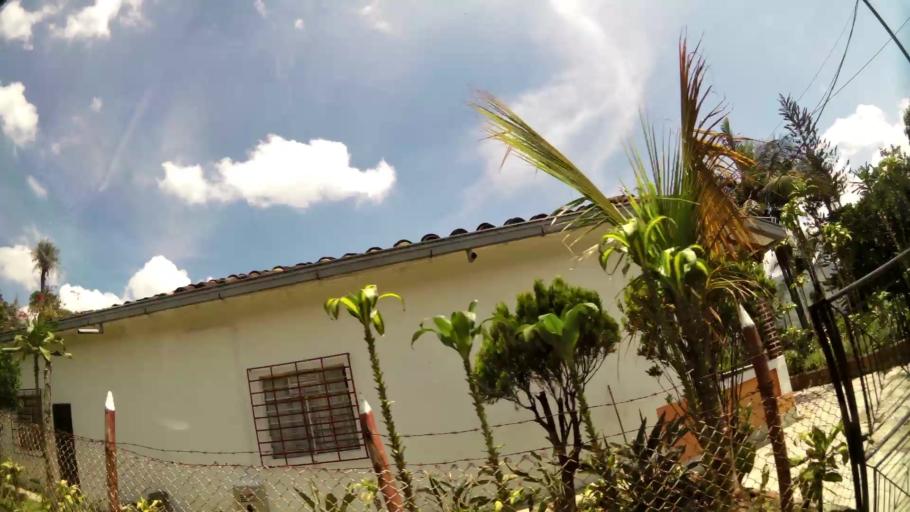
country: CO
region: Antioquia
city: La Estrella
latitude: 6.1792
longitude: -75.6559
